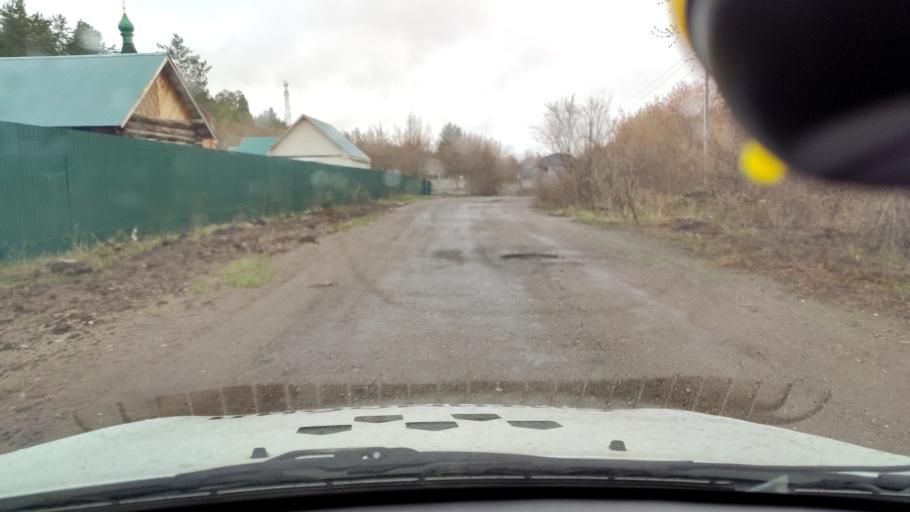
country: RU
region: Samara
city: Tol'yatti
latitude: 53.5255
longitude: 49.3923
